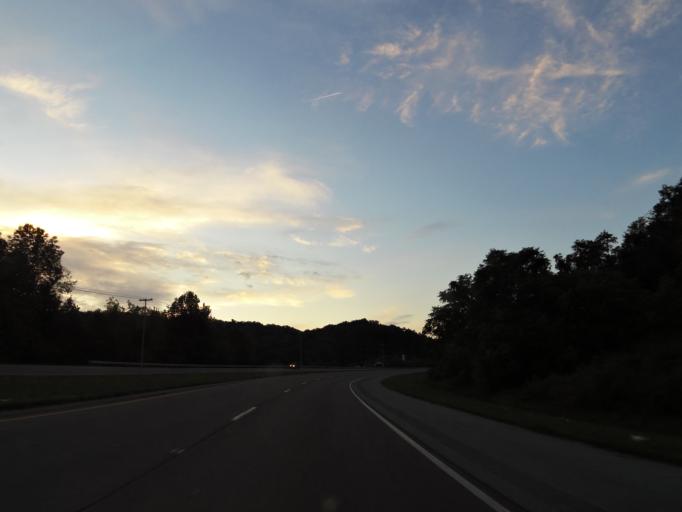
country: US
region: Tennessee
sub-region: Carter County
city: Elizabethton
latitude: 36.3629
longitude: -82.2061
